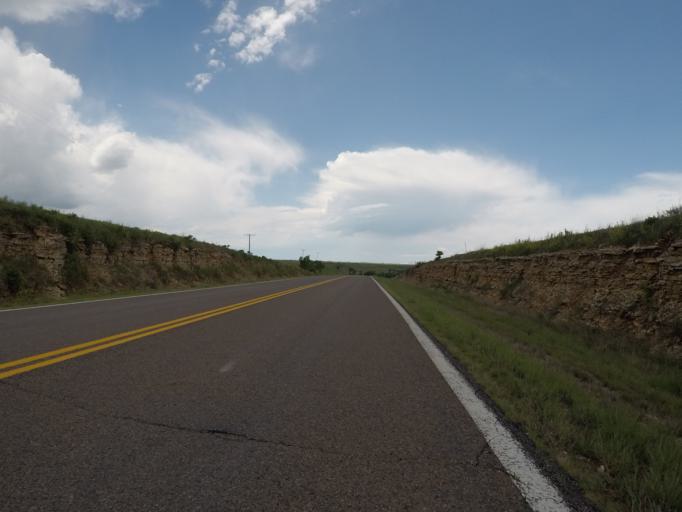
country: US
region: Kansas
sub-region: Wabaunsee County
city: Alma
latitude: 38.8698
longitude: -96.3367
